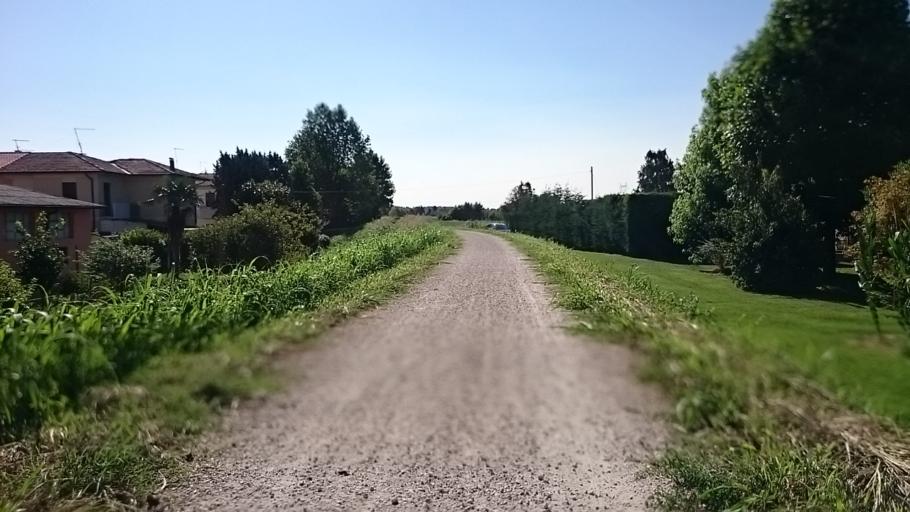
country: IT
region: Veneto
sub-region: Provincia di Vicenza
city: Villaganzerla
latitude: 45.4625
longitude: 11.6370
